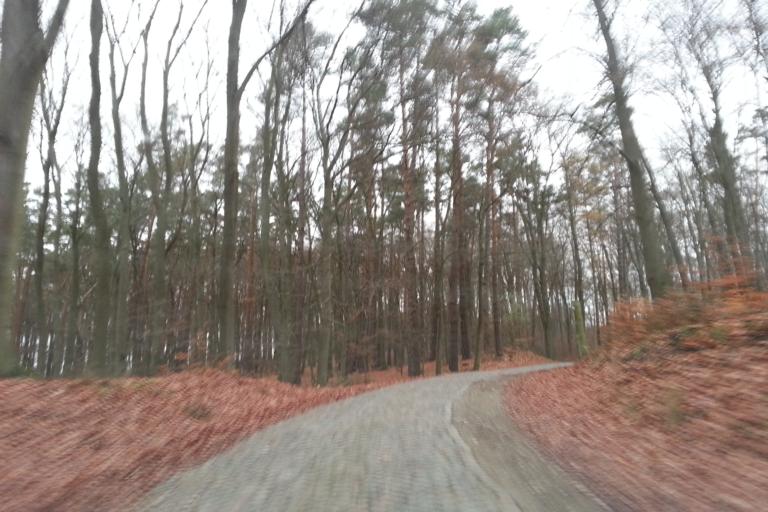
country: DE
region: Mecklenburg-Vorpommern
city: Ferdinandshof
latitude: 53.5908
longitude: 13.8413
